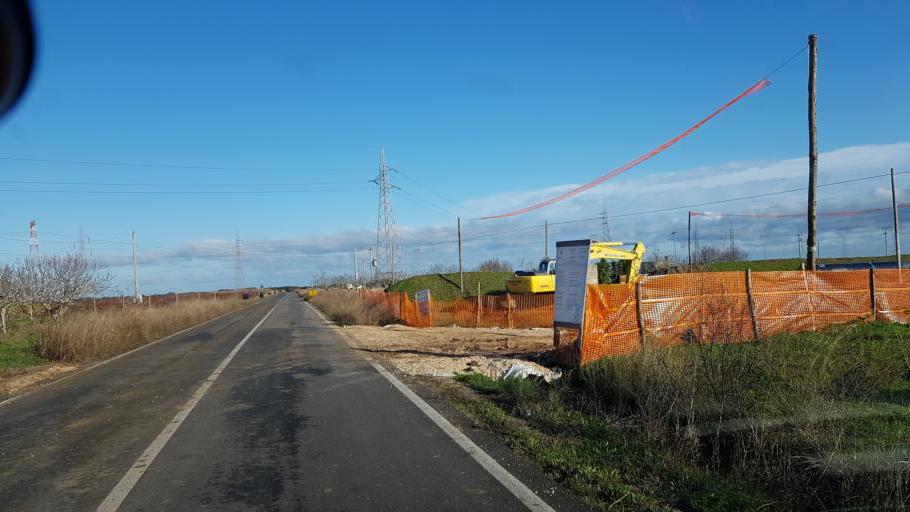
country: IT
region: Apulia
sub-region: Provincia di Brindisi
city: Tuturano
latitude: 40.5526
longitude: 17.9469
